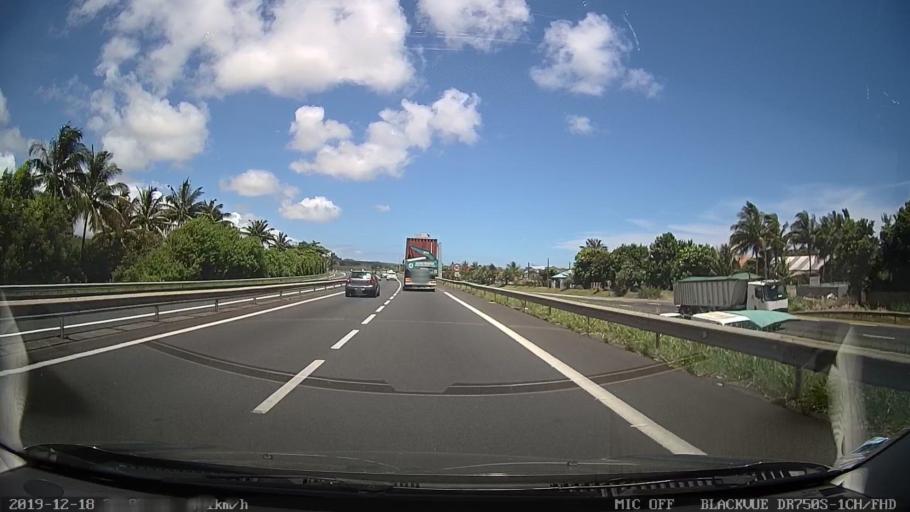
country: RE
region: Reunion
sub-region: Reunion
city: Sainte-Suzanne
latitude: -20.9163
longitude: 55.6226
